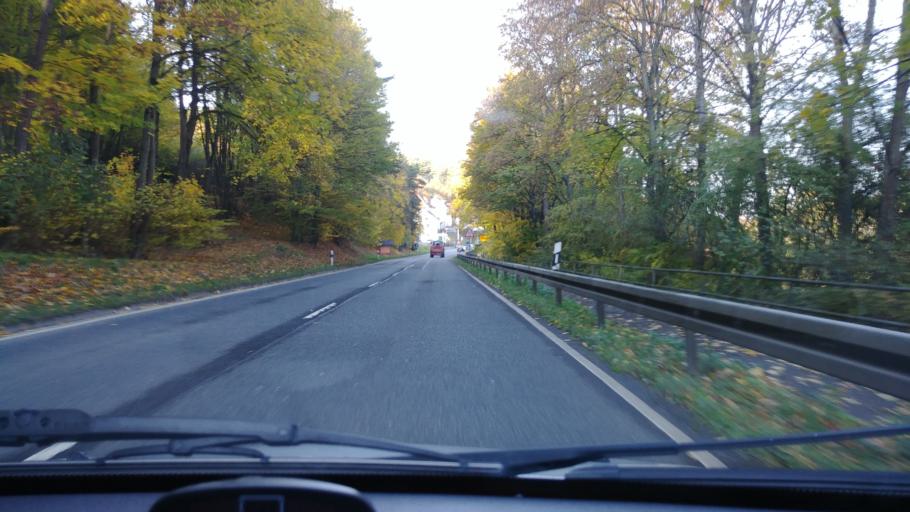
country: DE
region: Rheinland-Pfalz
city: Schiesheim
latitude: 50.2471
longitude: 8.0611
